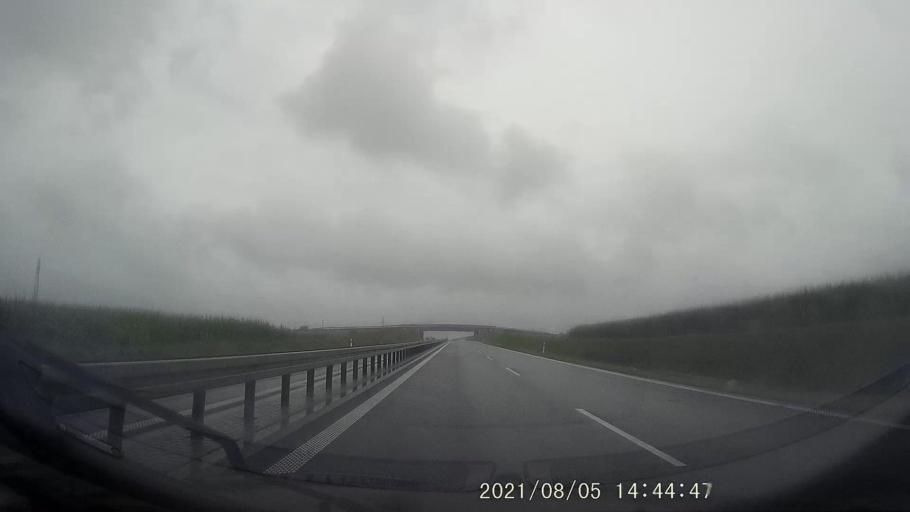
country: PL
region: Opole Voivodeship
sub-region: Powiat nyski
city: Nysa
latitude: 50.4962
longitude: 17.3727
